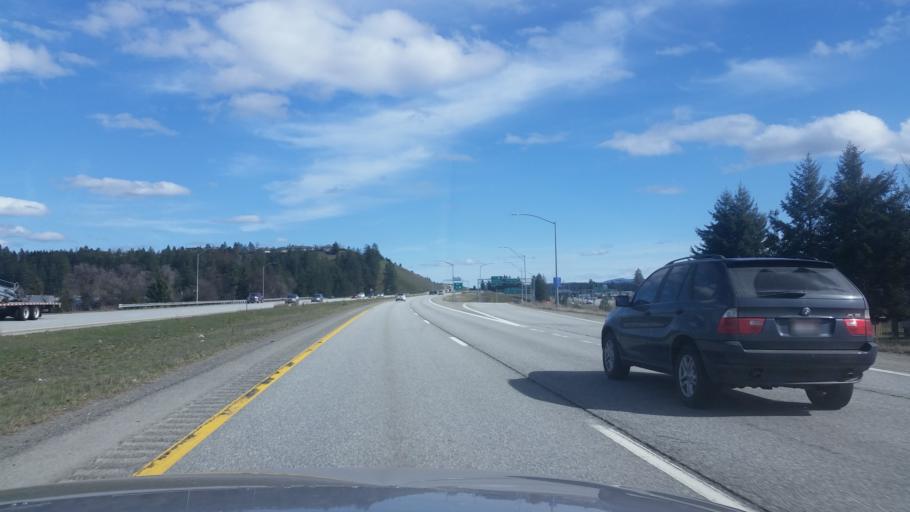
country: US
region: Idaho
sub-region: Kootenai County
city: Post Falls
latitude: 47.7122
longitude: -116.9033
